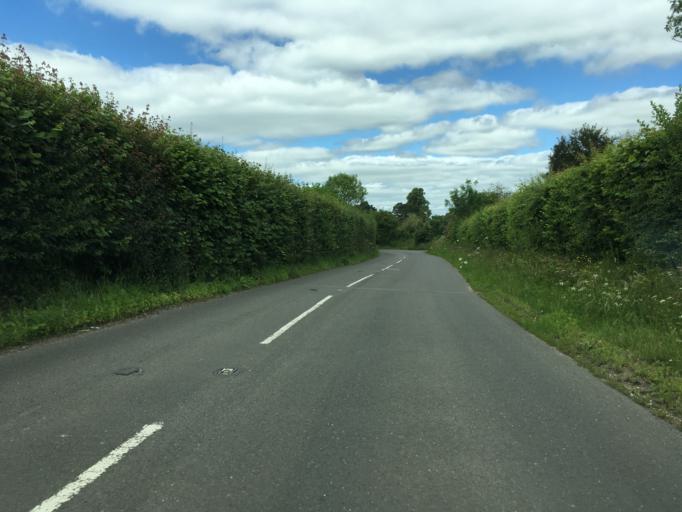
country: GB
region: England
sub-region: West Berkshire
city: Winterbourne
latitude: 51.4185
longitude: -1.3585
